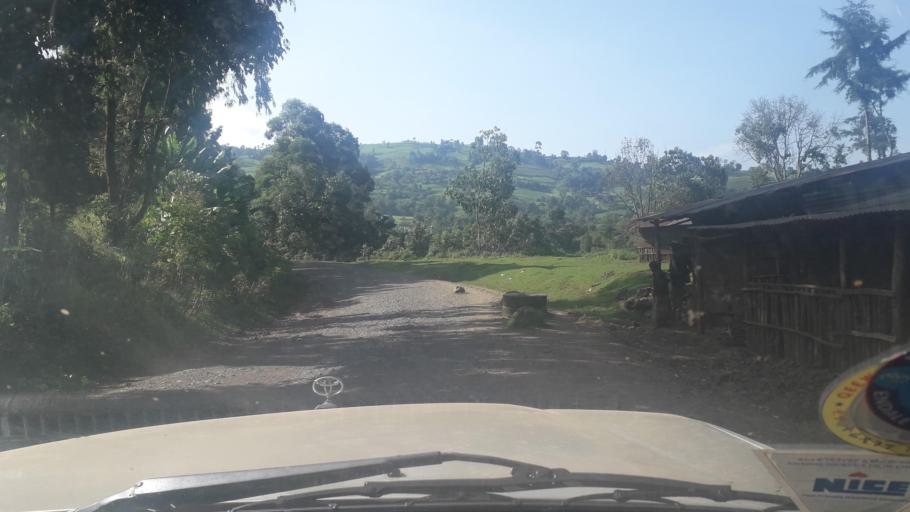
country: ET
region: Oromiya
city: Jima
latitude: 7.3845
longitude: 36.8675
